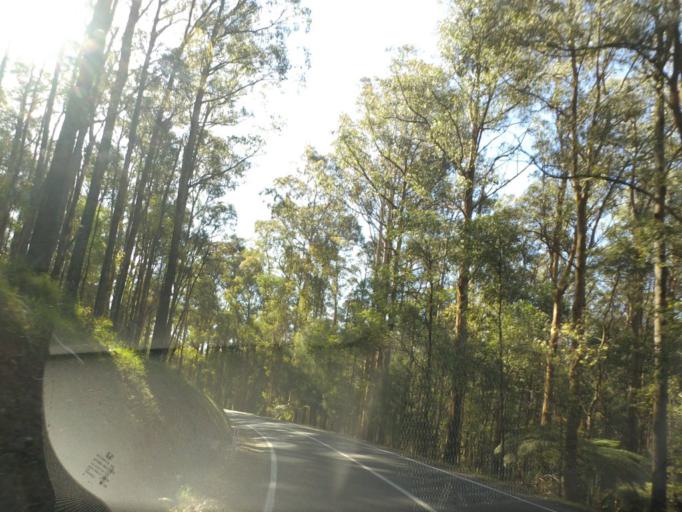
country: AU
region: Victoria
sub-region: Yarra Ranges
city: Millgrove
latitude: -37.8692
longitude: 145.7772
